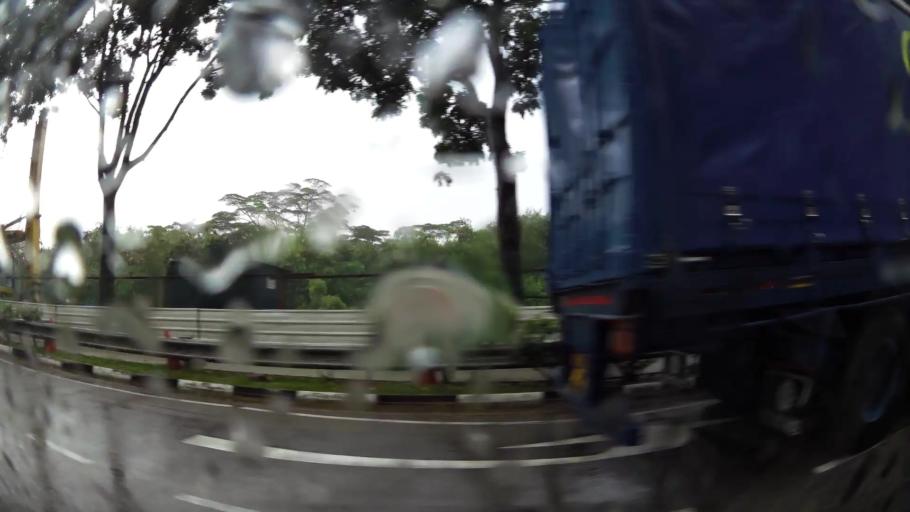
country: SG
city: Singapore
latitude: 1.3704
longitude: 103.9323
